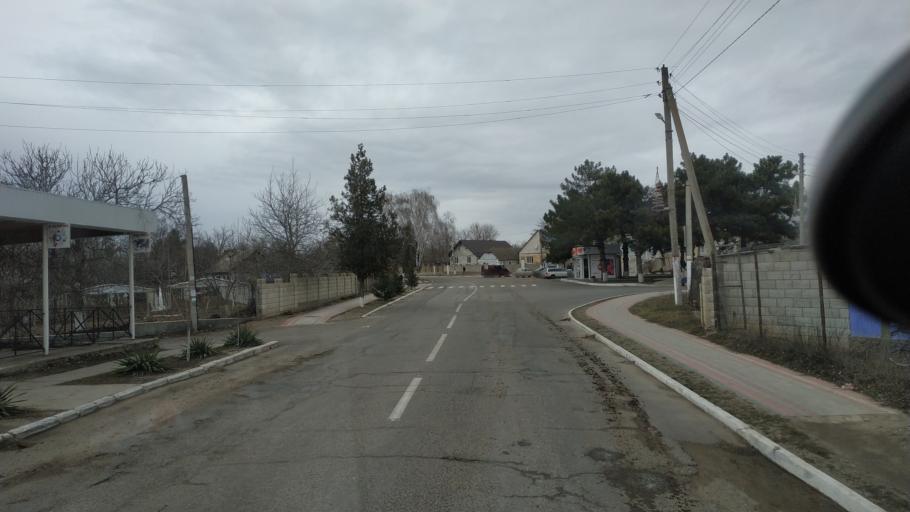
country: MD
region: Telenesti
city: Cocieri
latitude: 47.3057
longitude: 29.1120
